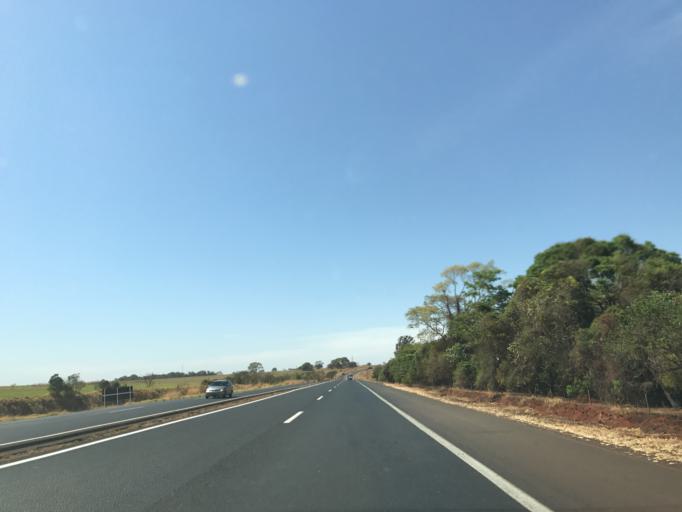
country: BR
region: Minas Gerais
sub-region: Centralina
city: Centralina
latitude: -18.7484
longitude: -49.0871
